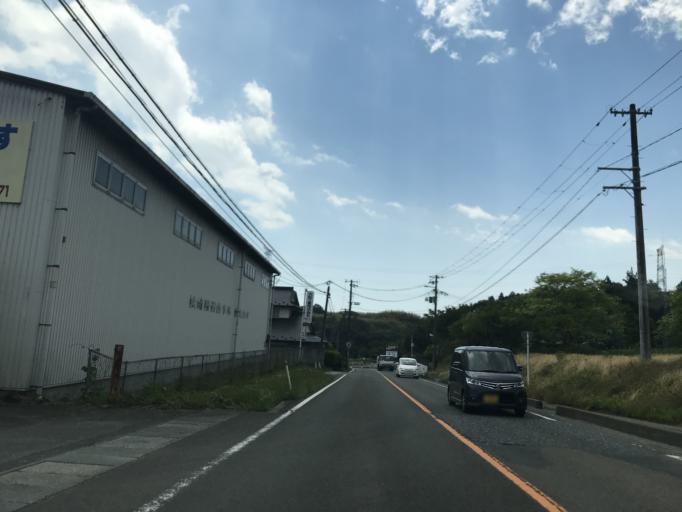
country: JP
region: Miyagi
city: Matsushima
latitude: 38.4165
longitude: 141.0618
